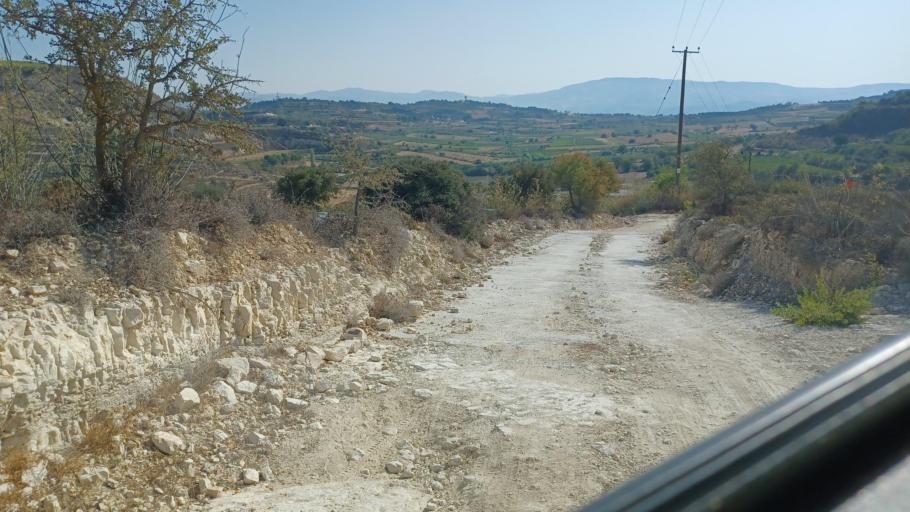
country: CY
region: Pafos
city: Tala
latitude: 34.8667
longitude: 32.4821
